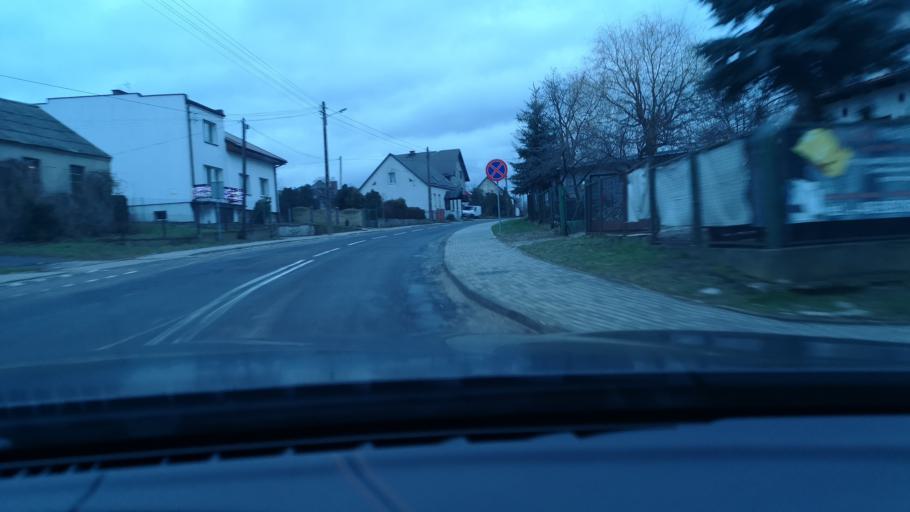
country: PL
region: Greater Poland Voivodeship
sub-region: Powiat slupecki
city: Orchowo
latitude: 52.5989
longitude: 18.0401
